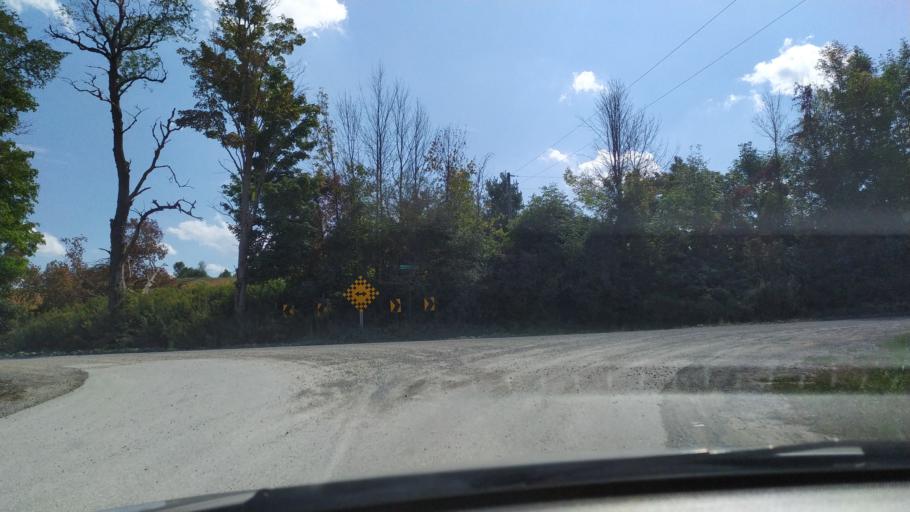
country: CA
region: Ontario
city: Stratford
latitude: 43.2904
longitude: -80.9370
